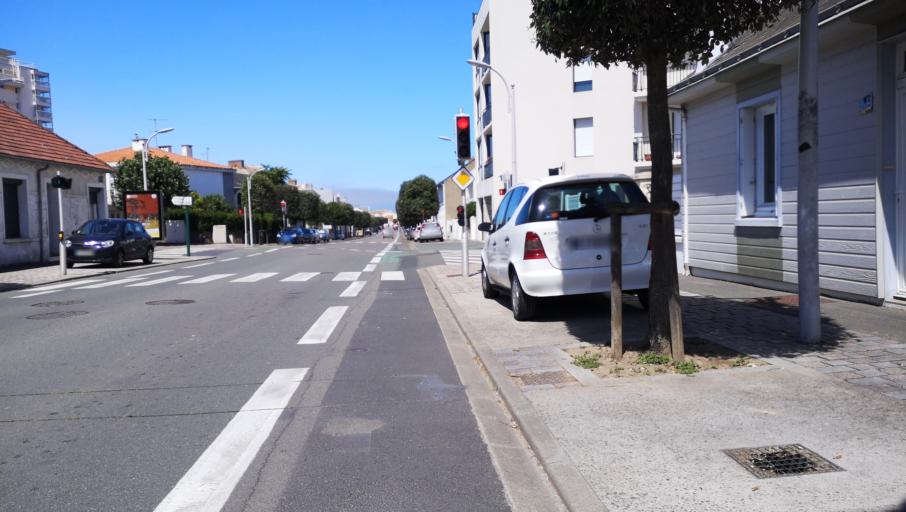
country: FR
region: Pays de la Loire
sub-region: Departement de la Vendee
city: Les Sables-d'Olonne
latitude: 46.4945
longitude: -1.7660
